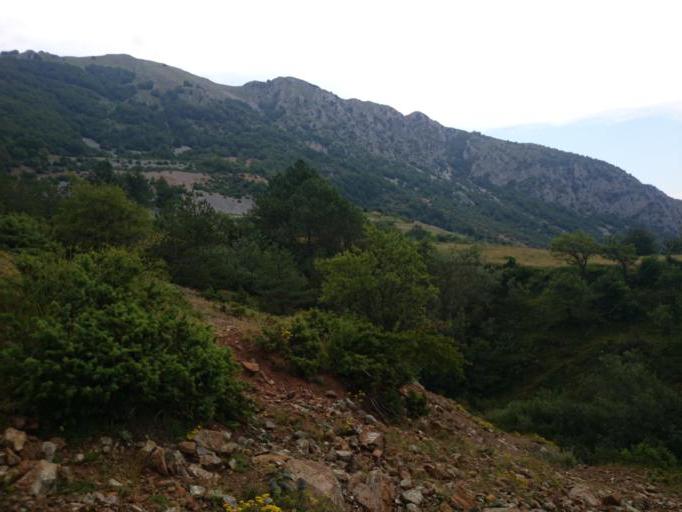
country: AL
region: Diber
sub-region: Rrethi i Dibres
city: Fushe-Lure
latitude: 41.7688
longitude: 20.2267
